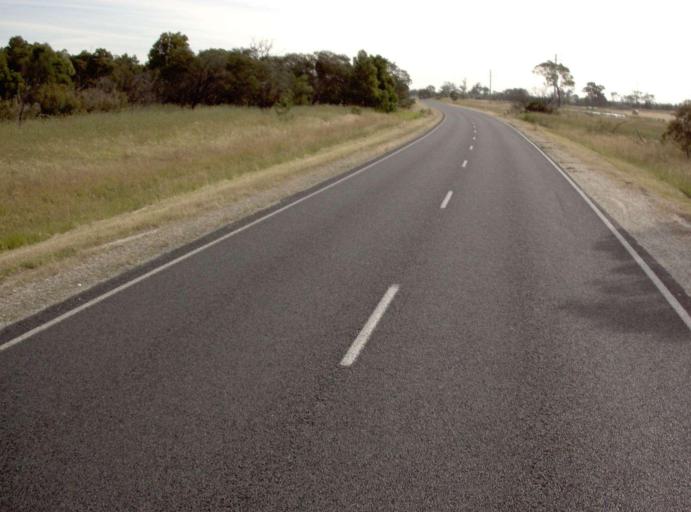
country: AU
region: Victoria
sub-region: Latrobe
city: Traralgon
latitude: -38.1094
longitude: 146.5878
